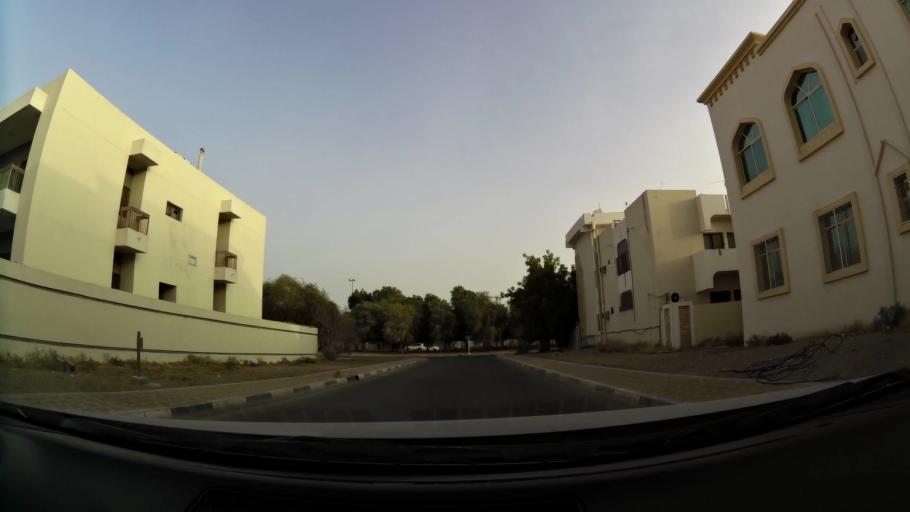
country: AE
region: Abu Dhabi
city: Al Ain
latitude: 24.2432
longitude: 55.7219
